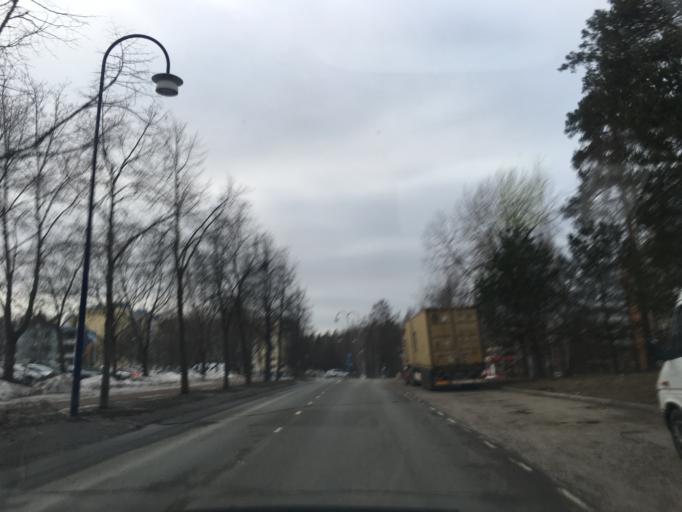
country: FI
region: Uusimaa
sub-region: Helsinki
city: Vantaa
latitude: 60.3234
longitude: 25.0783
